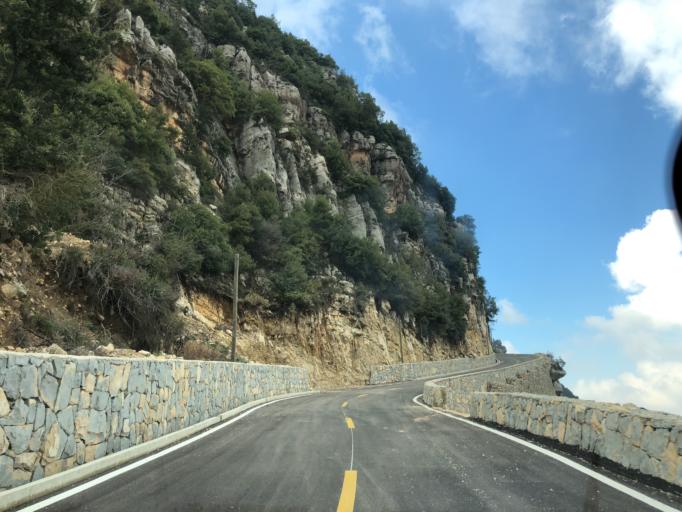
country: LB
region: Liban-Nord
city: Amioun
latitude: 34.2073
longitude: 35.8318
